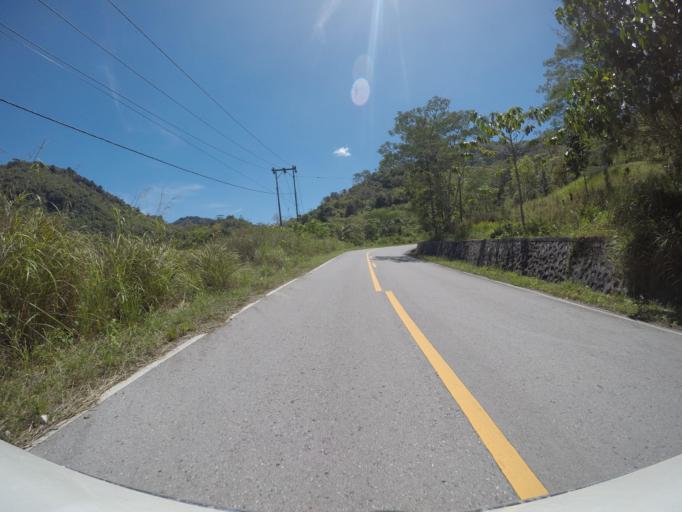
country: TL
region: Manatuto
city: Manatuto
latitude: -8.7682
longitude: 125.9665
